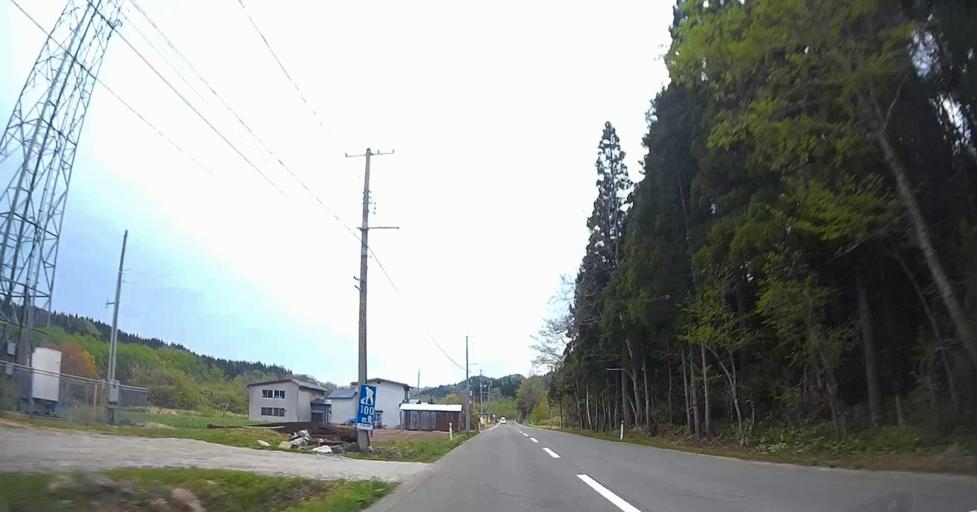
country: JP
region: Aomori
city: Goshogawara
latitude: 41.1307
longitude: 140.5196
